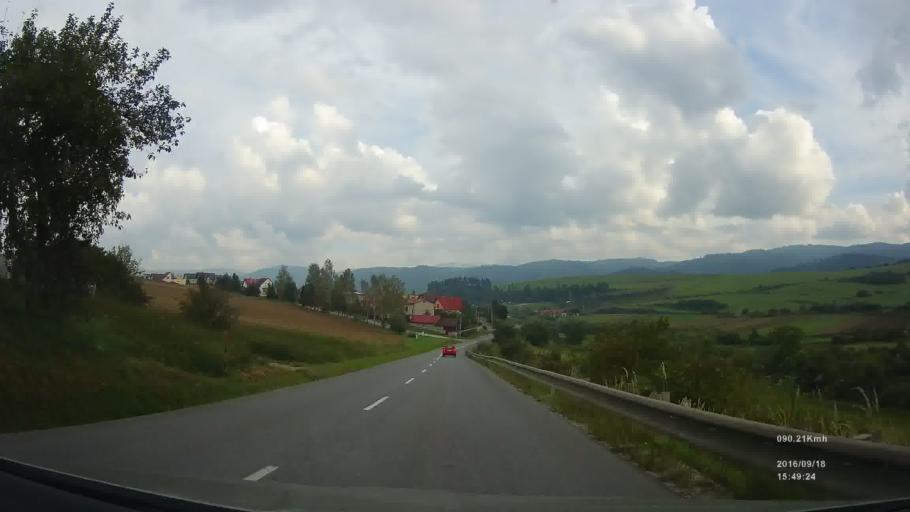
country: SK
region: Kosicky
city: Spisska Nova Ves
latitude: 48.9177
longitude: 20.6088
